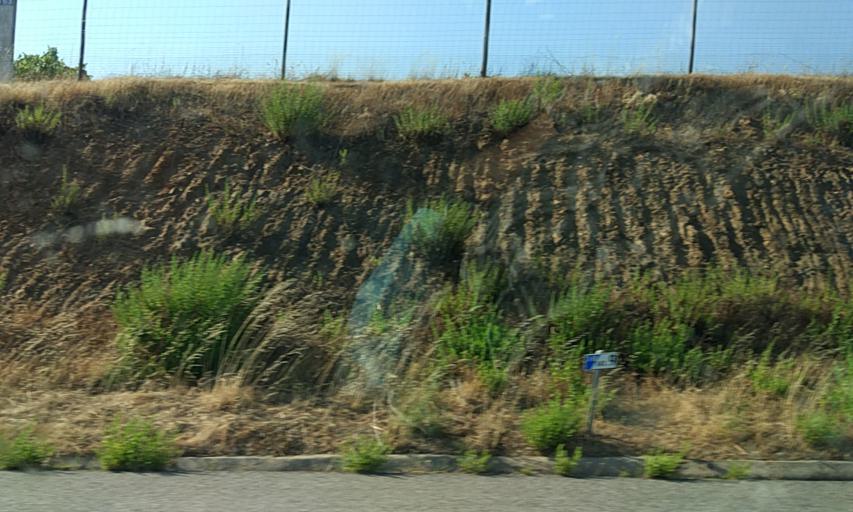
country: PT
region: Braganca
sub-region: Mirandela
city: Mirandela
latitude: 41.4639
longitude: -7.2492
